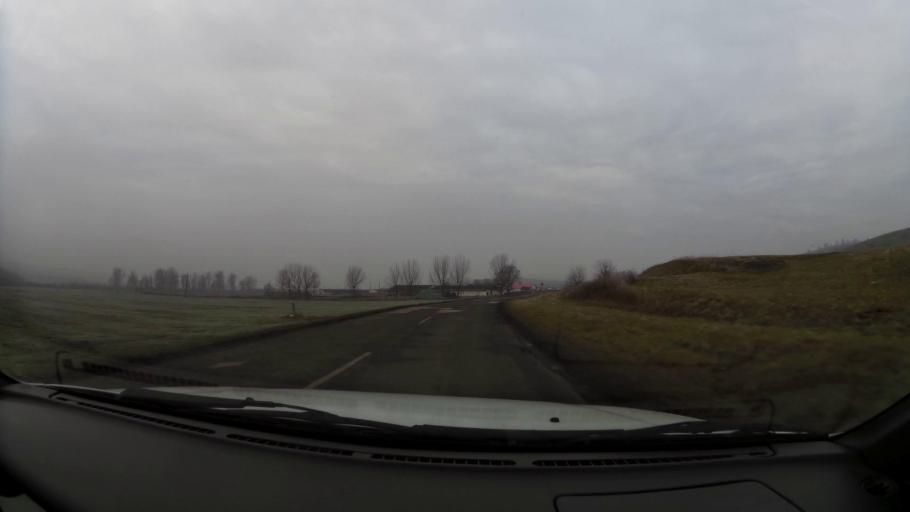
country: HU
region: Borsod-Abauj-Zemplen
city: Izsofalva
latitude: 48.2953
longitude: 20.6581
